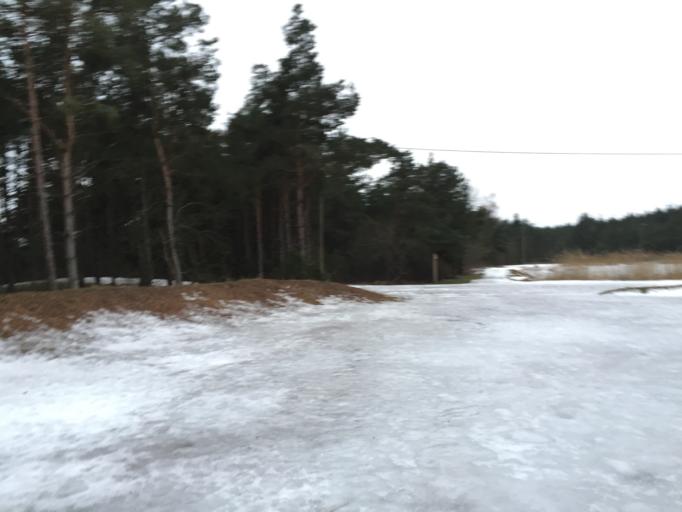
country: EE
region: Saare
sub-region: Kuressaare linn
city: Kuressaare
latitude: 58.2453
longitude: 22.5035
